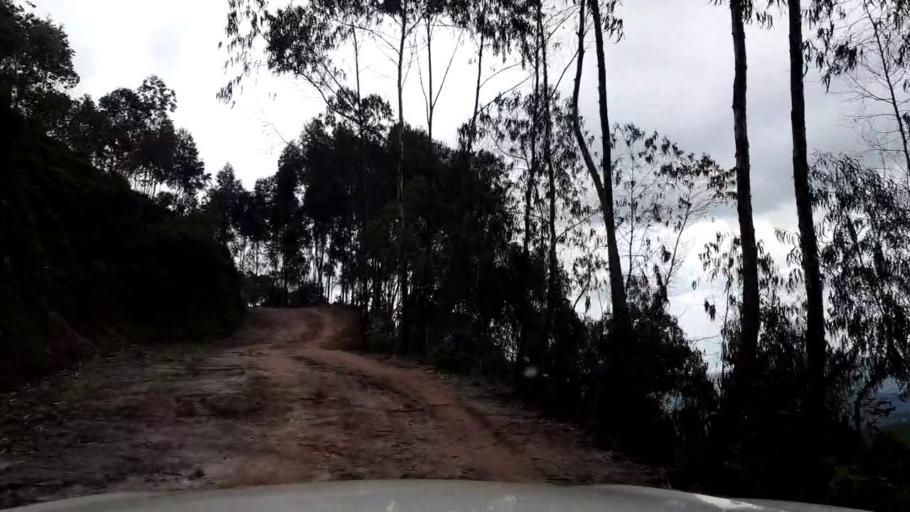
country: RW
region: Western Province
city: Kibuye
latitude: -1.9694
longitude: 29.4868
